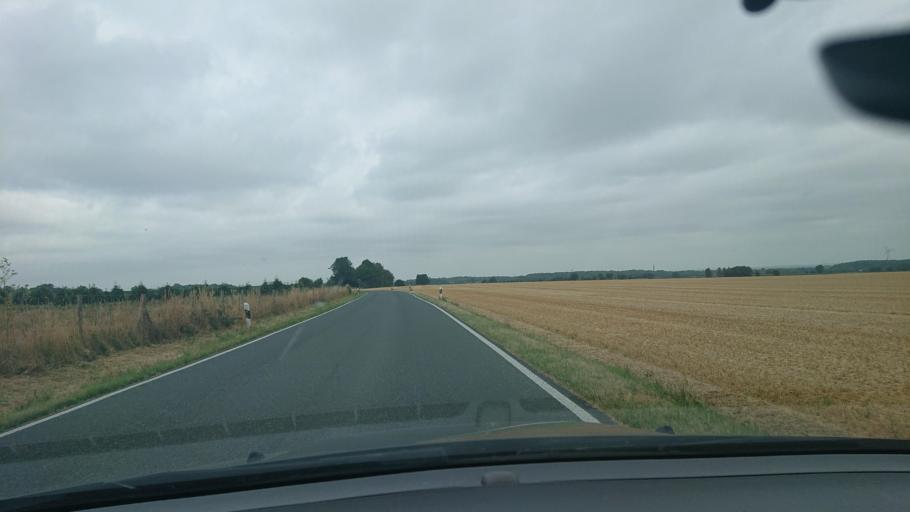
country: DE
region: North Rhine-Westphalia
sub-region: Regierungsbezirk Arnsberg
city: Bad Sassendorf
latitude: 51.5586
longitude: 8.1574
